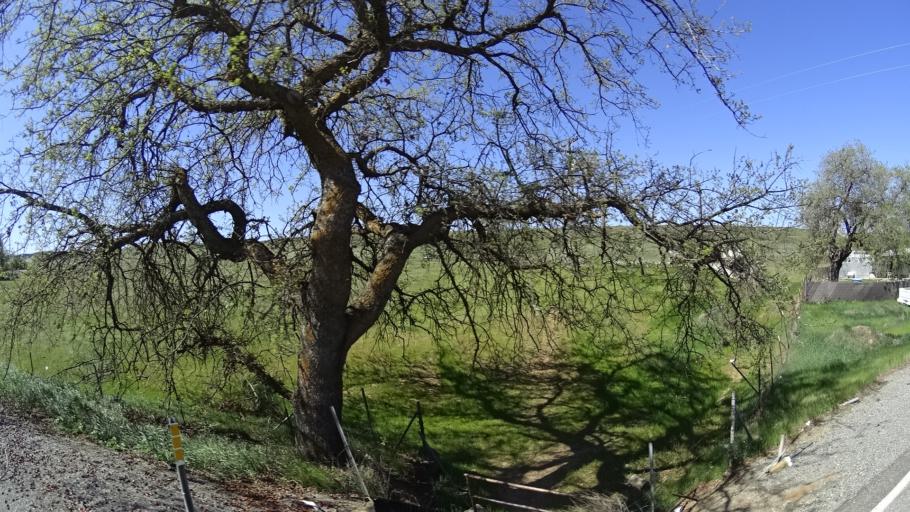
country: US
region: California
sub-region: Glenn County
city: Orland
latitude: 39.8079
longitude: -122.3303
